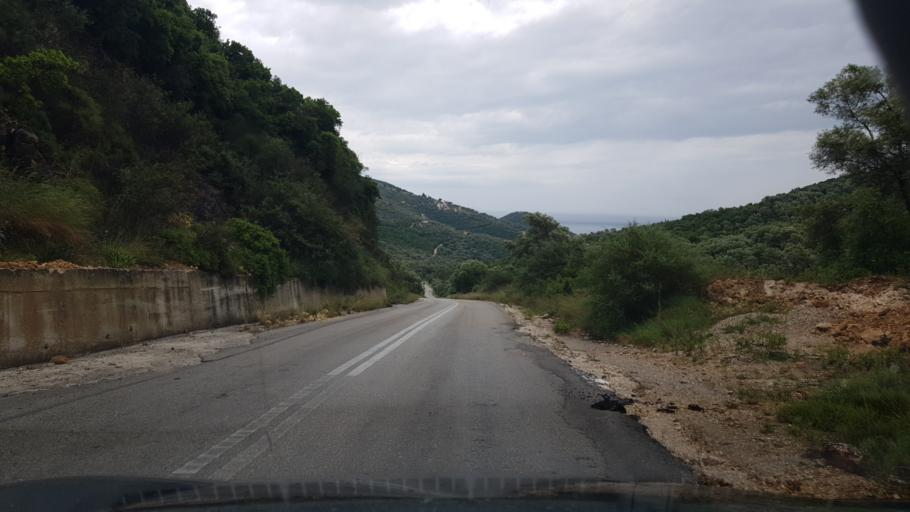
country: GR
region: Ionian Islands
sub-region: Lefkada
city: Nidri
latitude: 38.6319
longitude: 20.6692
